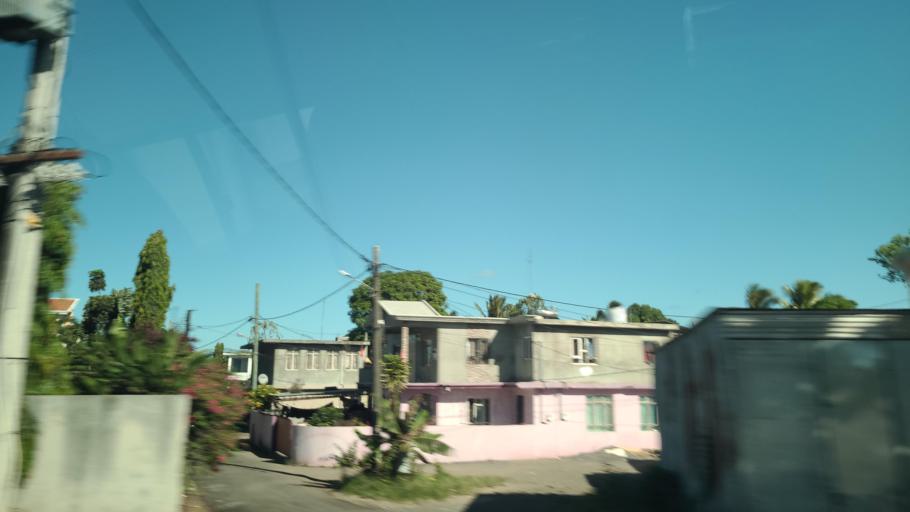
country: MU
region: Flacq
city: Poste de Flacq
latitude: -20.1657
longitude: 57.7361
